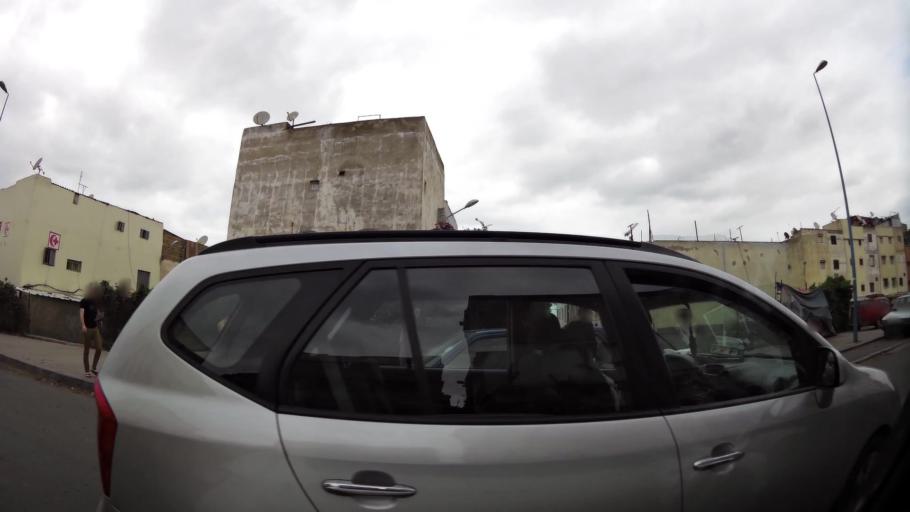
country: MA
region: Grand Casablanca
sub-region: Casablanca
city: Casablanca
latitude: 33.5847
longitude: -7.5622
